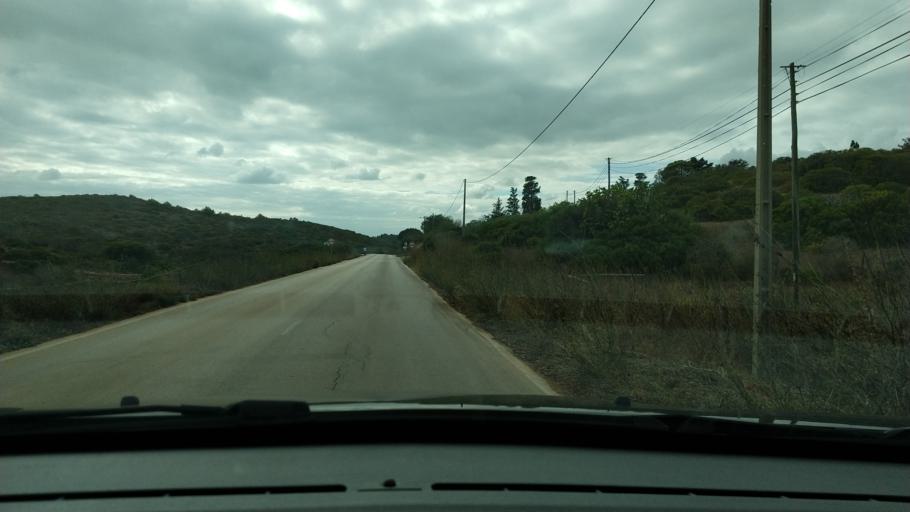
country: PT
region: Faro
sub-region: Lagos
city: Lagos
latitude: 37.0710
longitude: -8.7846
